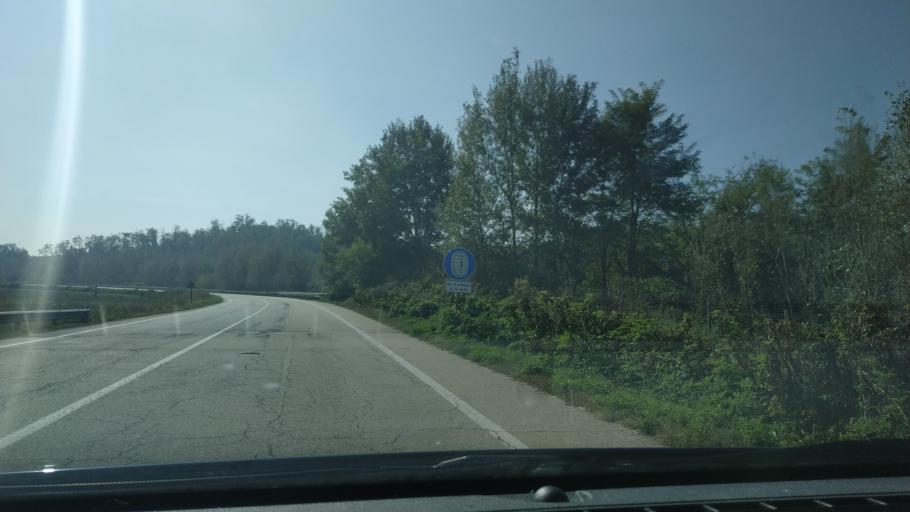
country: IT
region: Piedmont
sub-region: Provincia di Alessandria
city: Bozzole
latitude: 45.0430
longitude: 8.6211
